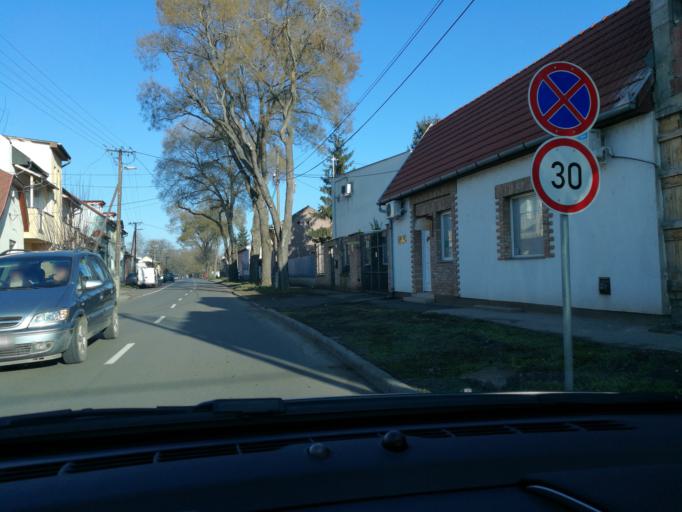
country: HU
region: Szabolcs-Szatmar-Bereg
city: Nyiregyhaza
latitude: 47.9614
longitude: 21.7211
